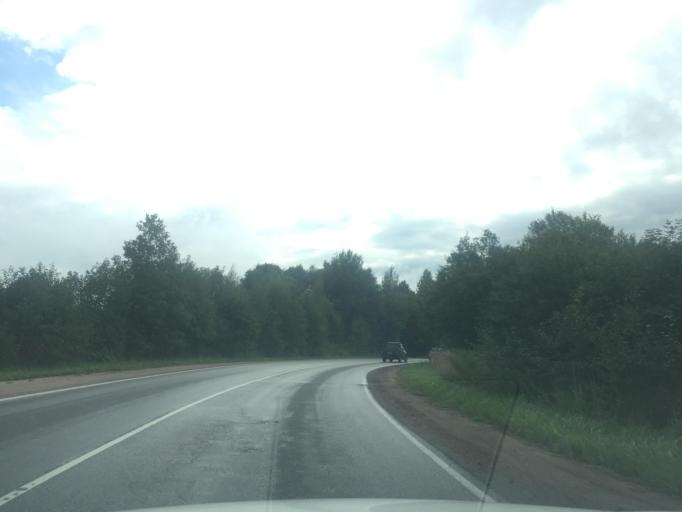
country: RU
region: Leningrad
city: Rozhdestveno
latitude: 59.3469
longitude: 29.9965
